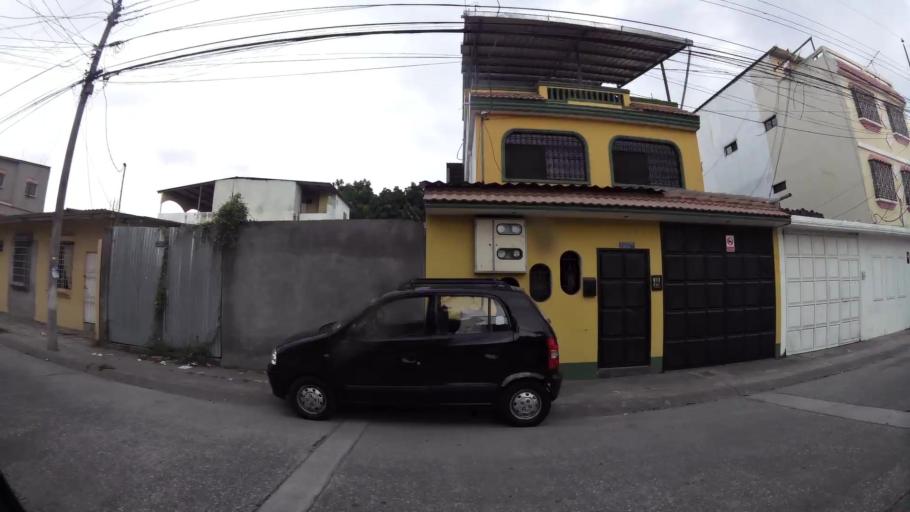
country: EC
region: Guayas
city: Eloy Alfaro
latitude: -2.1202
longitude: -79.8840
